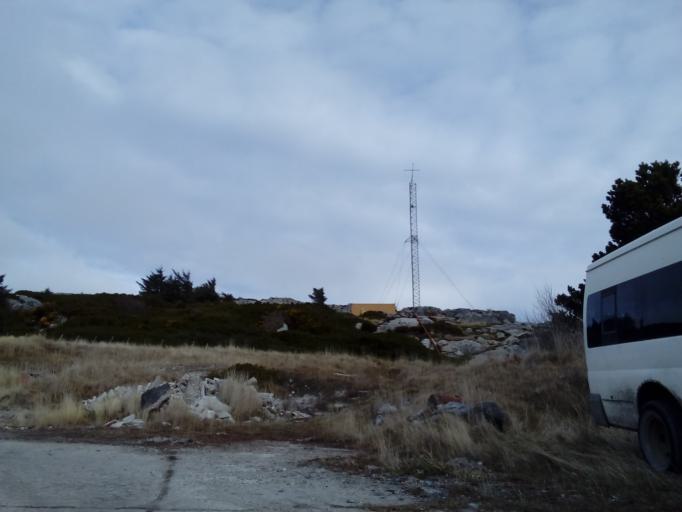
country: FK
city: Stanley
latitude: -51.6924
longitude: -57.8766
